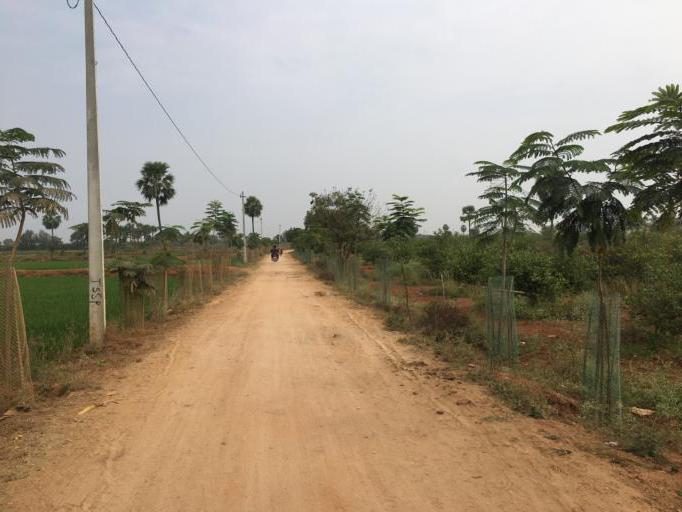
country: IN
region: Telangana
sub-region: Nalgonda
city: Nalgonda
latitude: 17.1606
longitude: 79.3908
